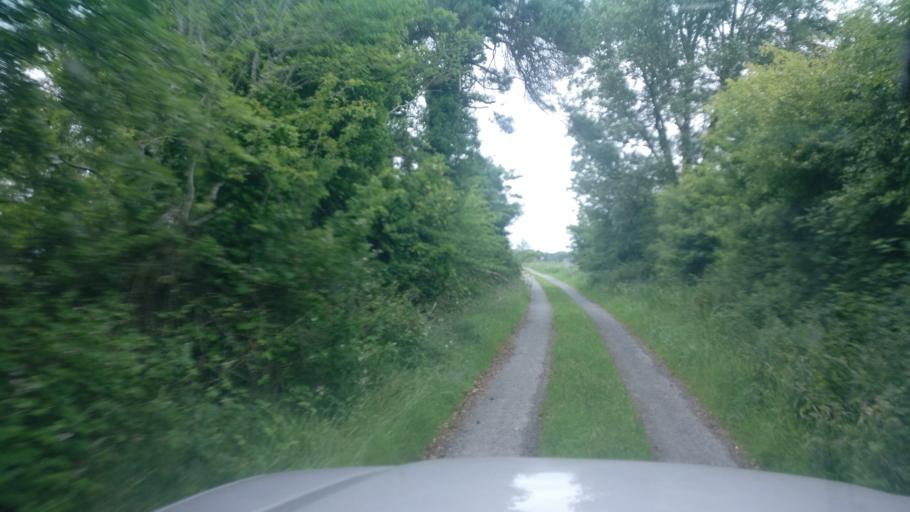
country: IE
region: Connaught
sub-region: County Galway
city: Ballinasloe
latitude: 53.2952
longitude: -8.3632
